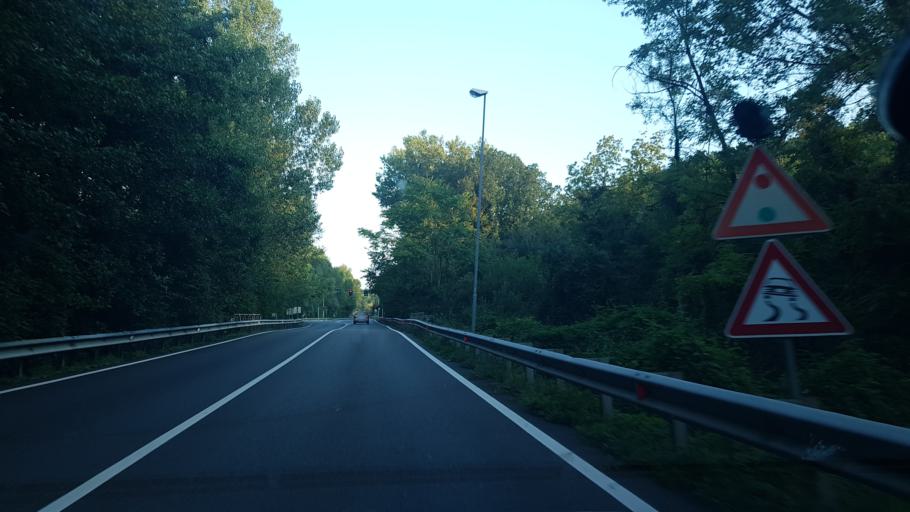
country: IT
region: Friuli Venezia Giulia
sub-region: Provincia di Trieste
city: Duino
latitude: 45.7927
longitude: 13.5855
